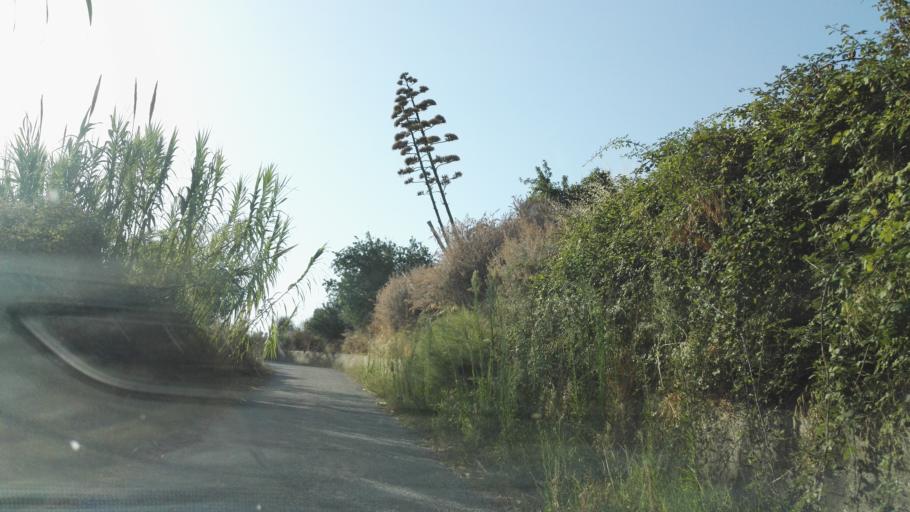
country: IT
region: Calabria
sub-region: Provincia di Reggio Calabria
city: Riace Marina
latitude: 38.3742
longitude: 16.4991
